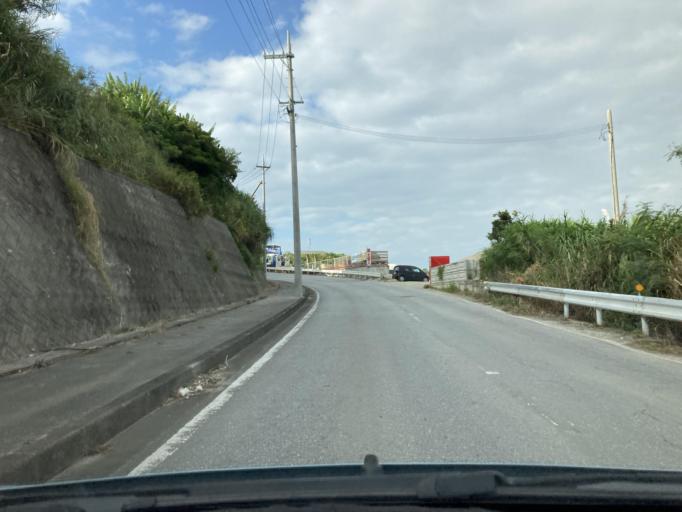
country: JP
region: Okinawa
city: Ginowan
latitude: 26.2241
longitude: 127.7369
